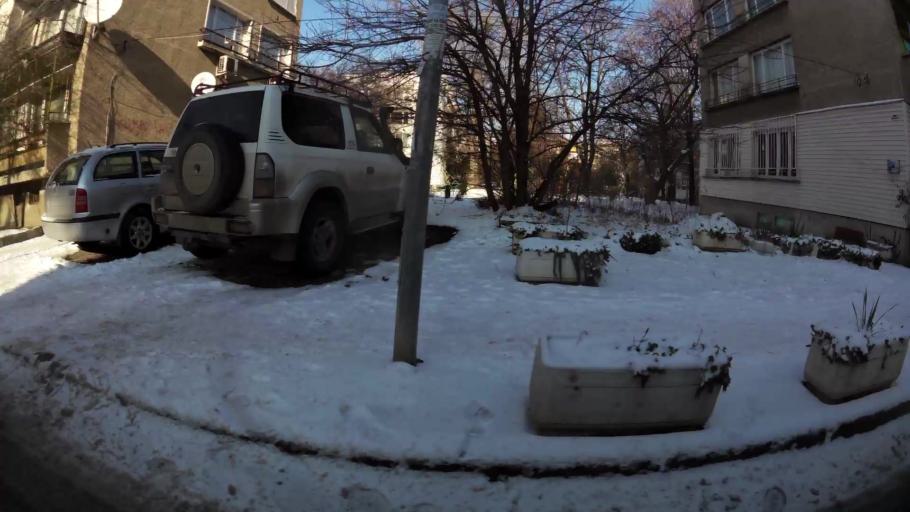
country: BG
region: Sofia-Capital
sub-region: Stolichna Obshtina
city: Sofia
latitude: 42.6725
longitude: 23.3592
